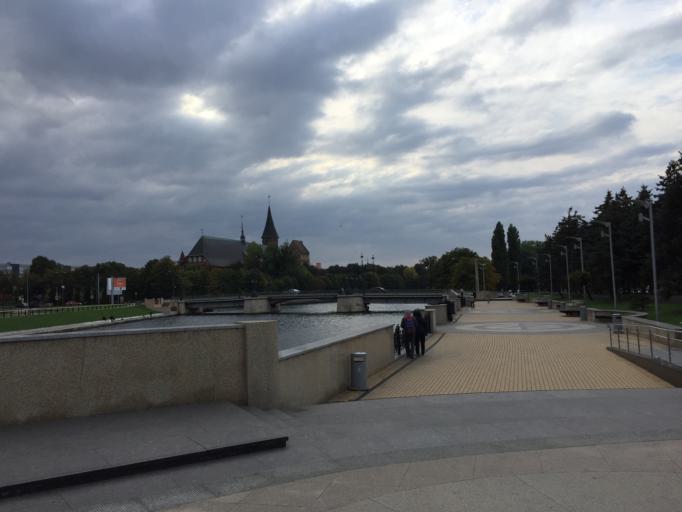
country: RU
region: Kaliningrad
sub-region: Gorod Kaliningrad
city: Kaliningrad
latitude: 54.7077
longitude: 20.5168
